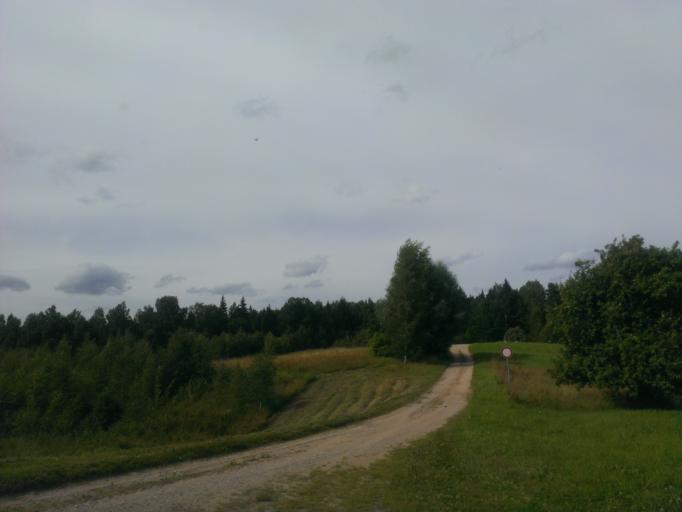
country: LV
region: Ligatne
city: Ligatne
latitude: 57.2294
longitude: 25.0126
